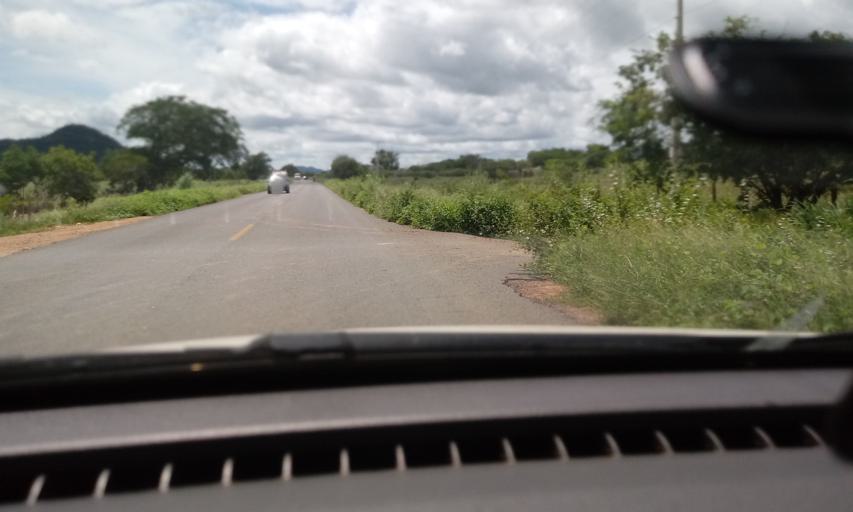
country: BR
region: Bahia
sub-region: Guanambi
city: Guanambi
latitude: -14.1335
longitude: -42.8495
